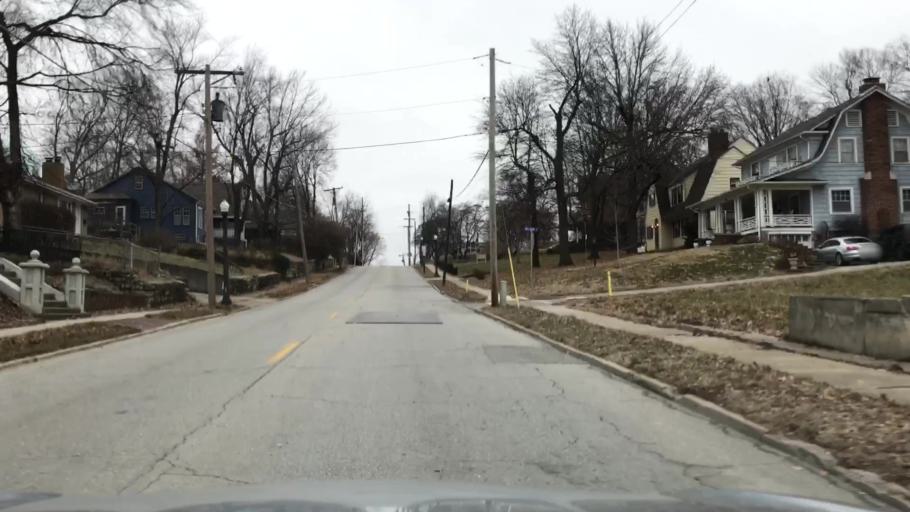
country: US
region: Missouri
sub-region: Clay County
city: Liberty
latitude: 39.2503
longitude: -94.4166
